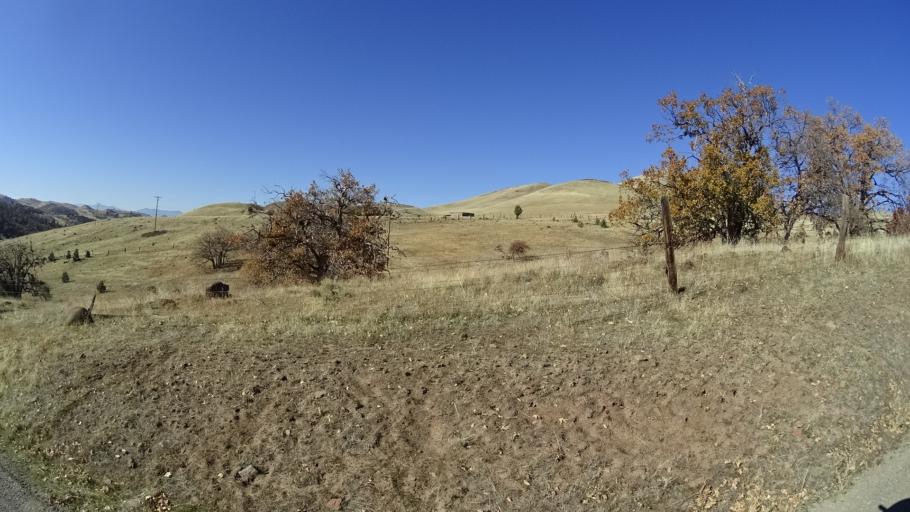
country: US
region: California
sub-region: Siskiyou County
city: Montague
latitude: 41.7965
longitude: -122.3361
